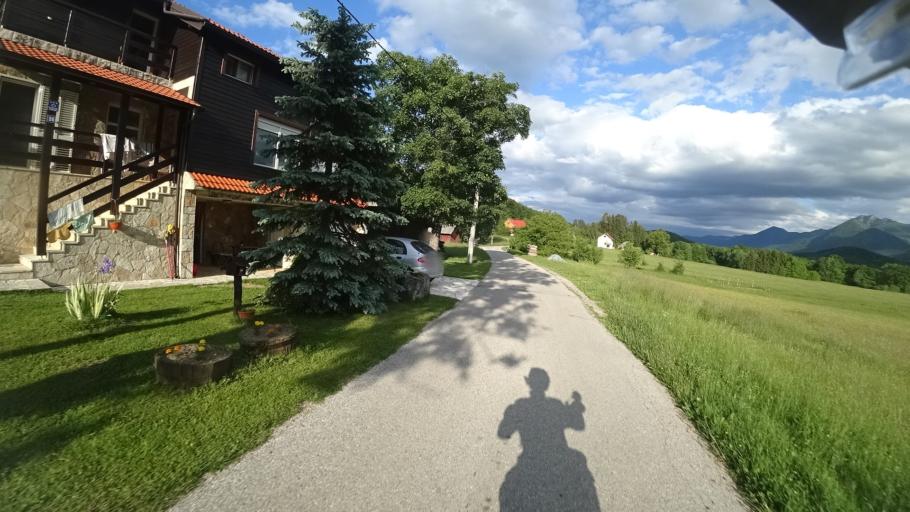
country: HR
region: Licko-Senjska
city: Gospic
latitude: 44.4912
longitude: 15.3068
